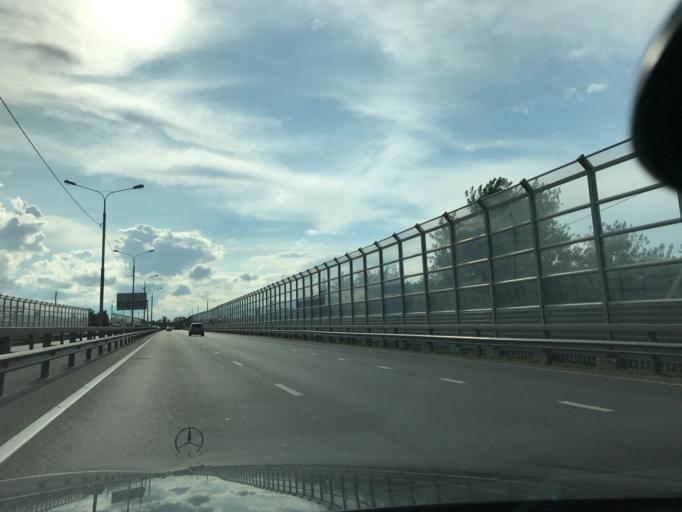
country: RU
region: Moskovskaya
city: Demikhovo
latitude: 55.8575
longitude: 38.8836
